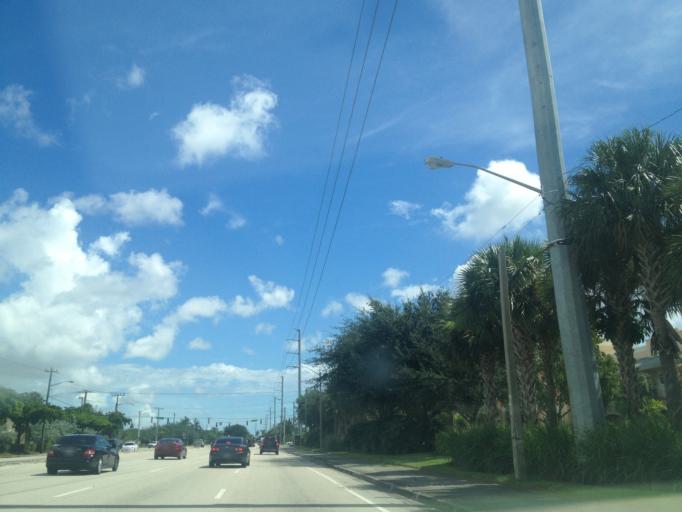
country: US
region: Florida
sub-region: Palm Beach County
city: Delray Beach
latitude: 26.4710
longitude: -80.0925
